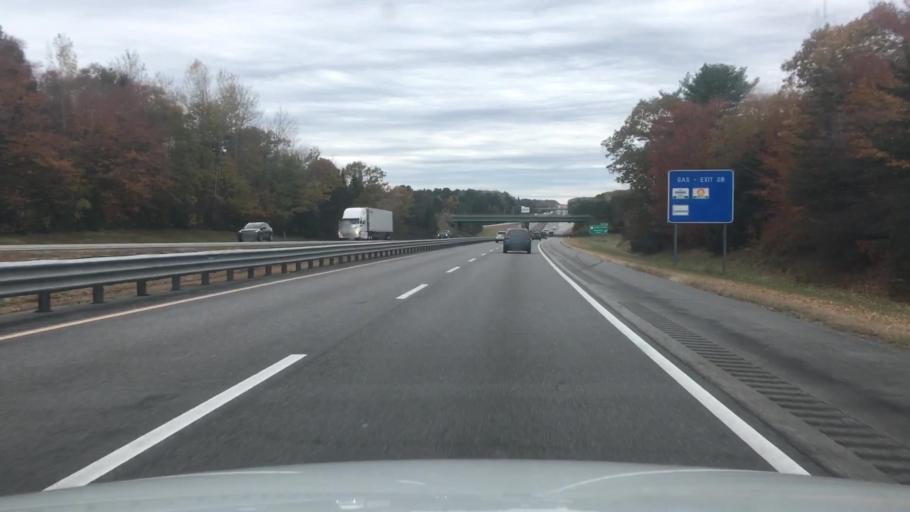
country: US
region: Maine
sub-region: Sagadahoc County
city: Topsham
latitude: 43.9191
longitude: -70.0163
